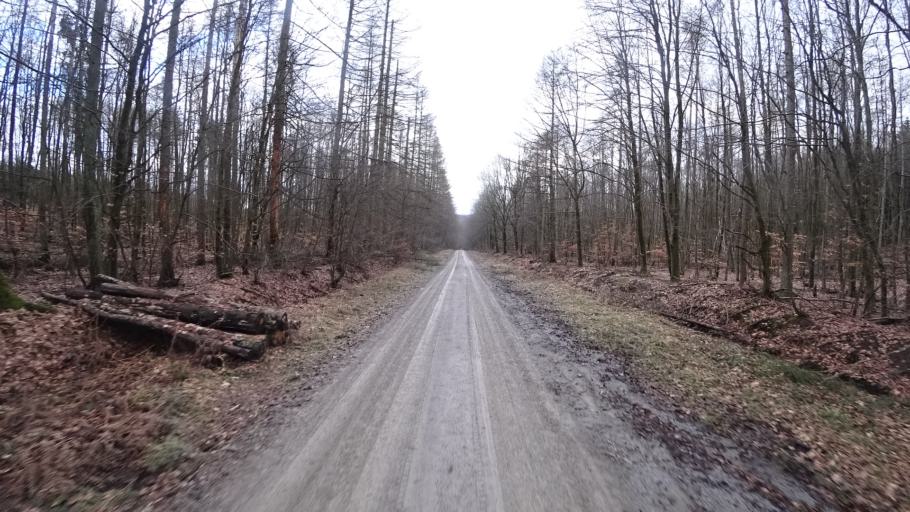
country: DE
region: Rheinland-Pfalz
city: Dernbach
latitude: 50.4271
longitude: 7.7661
